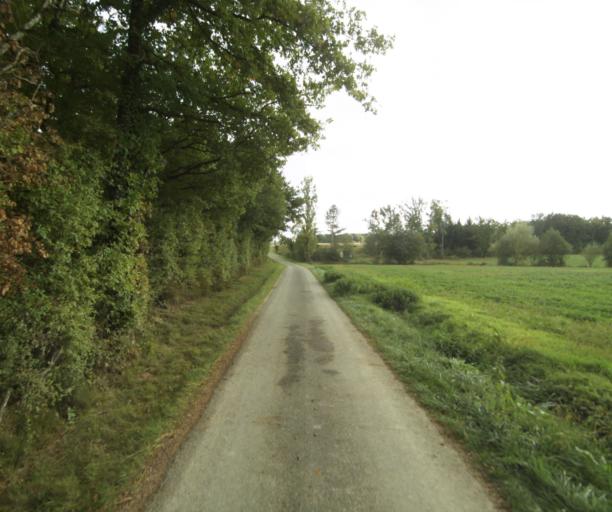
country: FR
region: Midi-Pyrenees
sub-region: Departement du Gers
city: Gondrin
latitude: 43.8598
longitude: 0.2208
